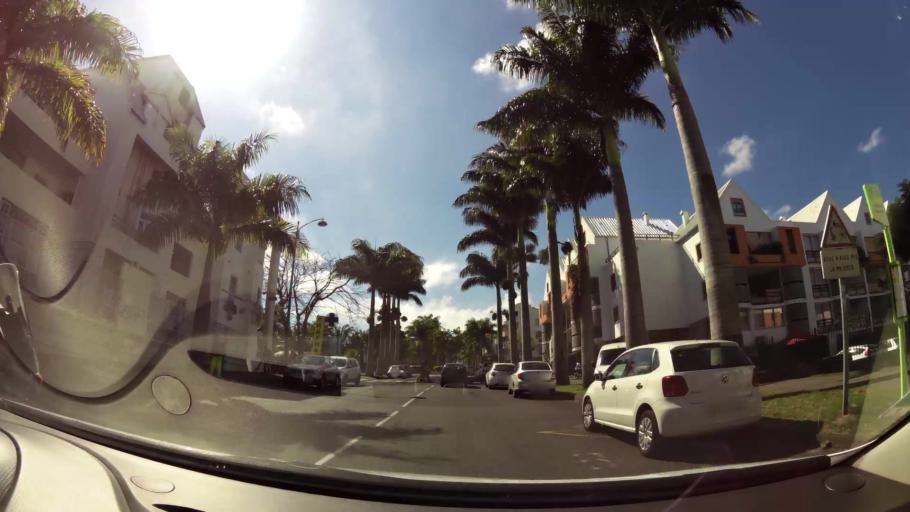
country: RE
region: Reunion
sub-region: Reunion
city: Le Tampon
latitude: -21.2775
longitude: 55.5029
